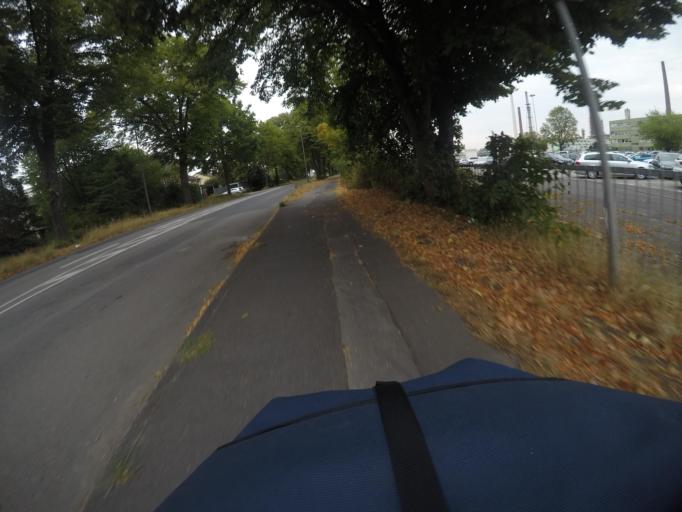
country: DE
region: North Rhine-Westphalia
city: Wesseling
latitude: 50.8544
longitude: 6.9752
